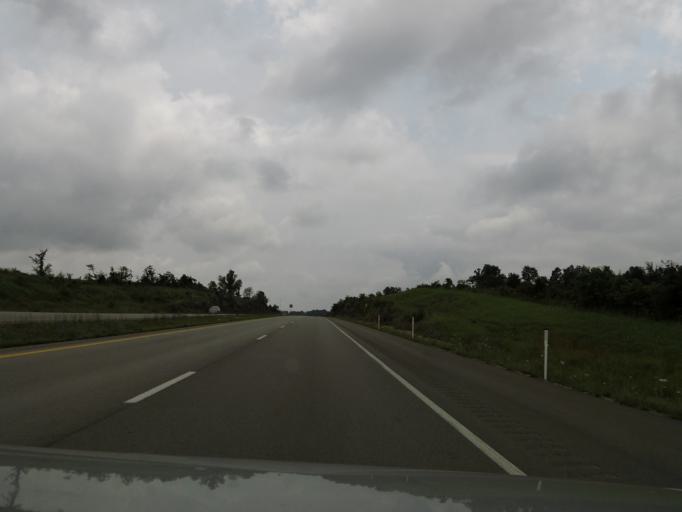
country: US
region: Kentucky
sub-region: Grayson County
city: Leitchfield
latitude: 37.4507
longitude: -86.3338
